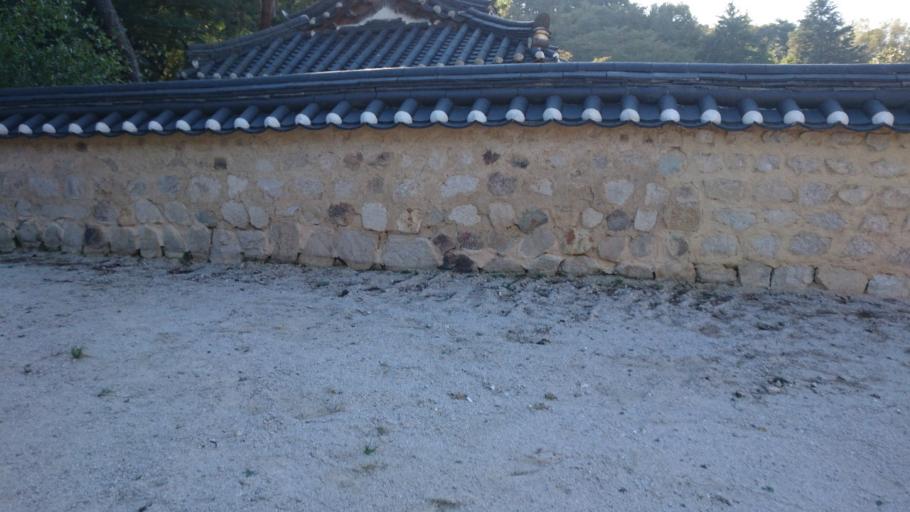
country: KR
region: Gyeongsangbuk-do
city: Kyonju
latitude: 35.8249
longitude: 129.2248
